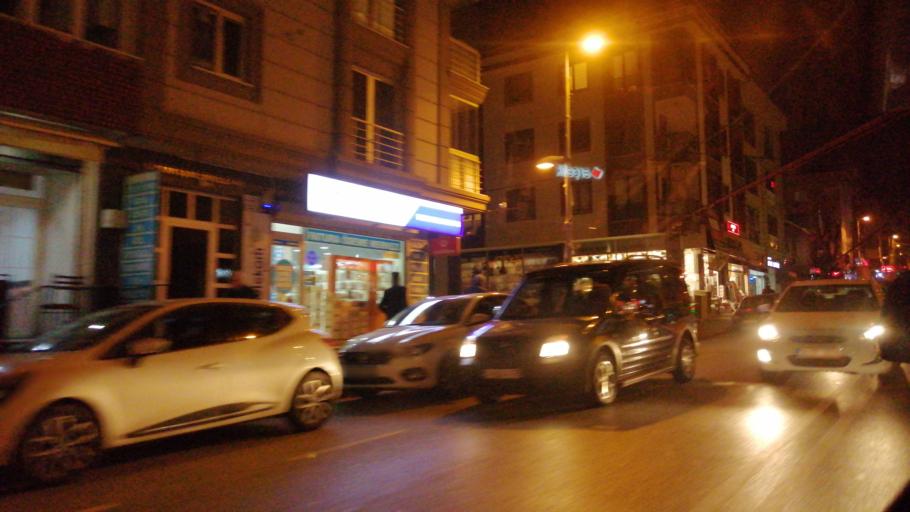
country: TR
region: Istanbul
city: Umraniye
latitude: 41.0122
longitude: 29.1281
